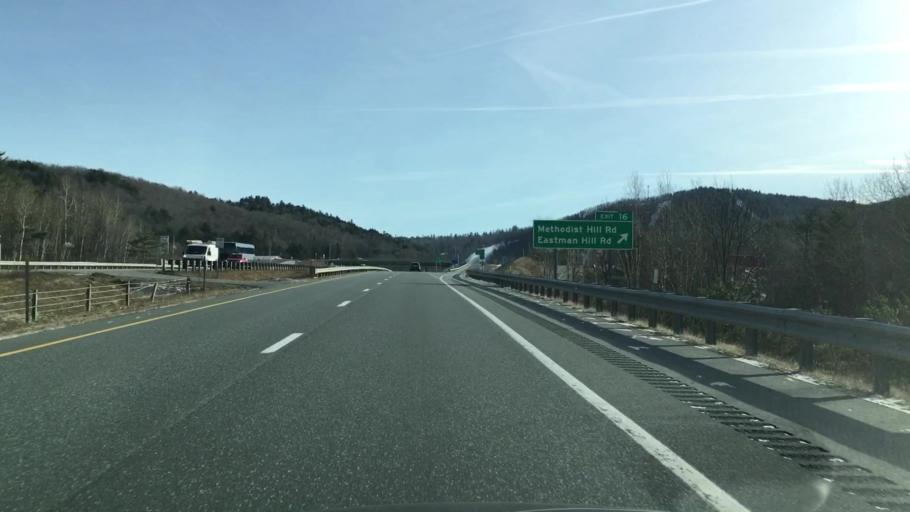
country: US
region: New Hampshire
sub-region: Grafton County
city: Enfield
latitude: 43.6134
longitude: -72.1921
